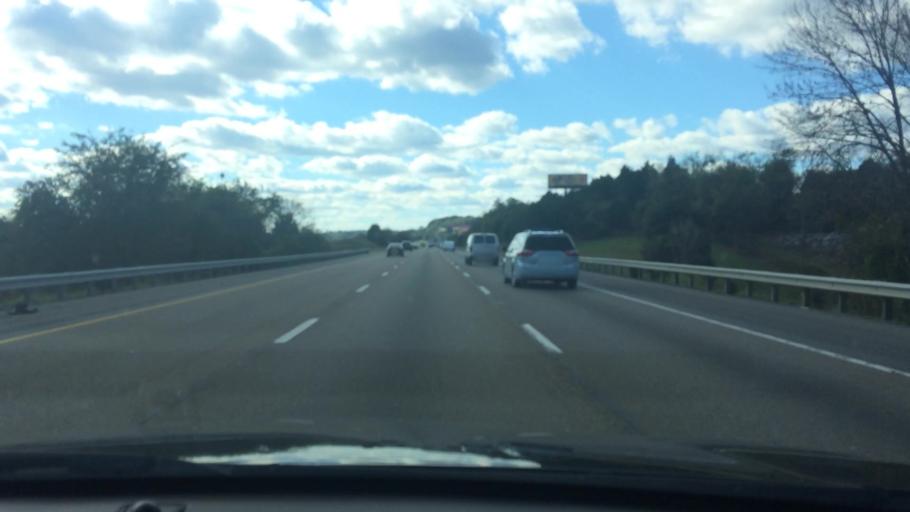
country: US
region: Tennessee
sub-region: Sevier County
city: Sevierville
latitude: 35.9857
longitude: -83.5924
